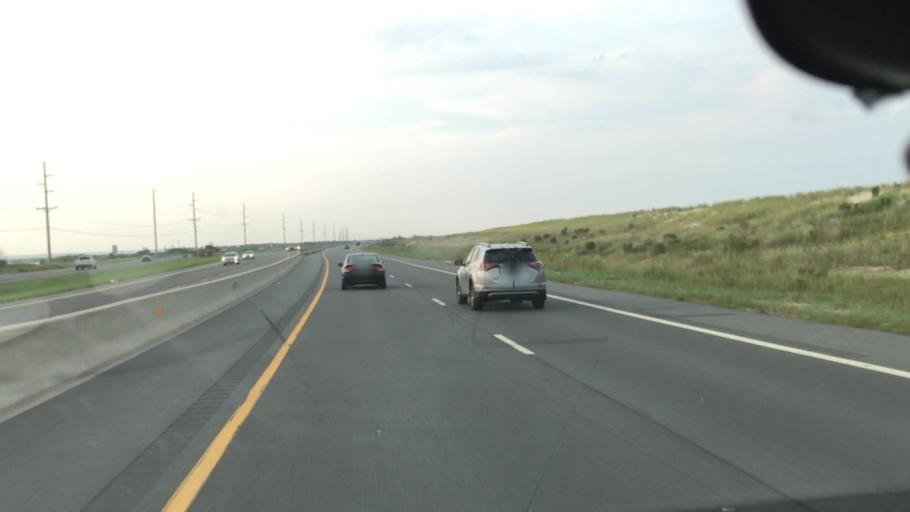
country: US
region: Delaware
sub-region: Sussex County
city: Ocean View
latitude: 38.6128
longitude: -75.0645
